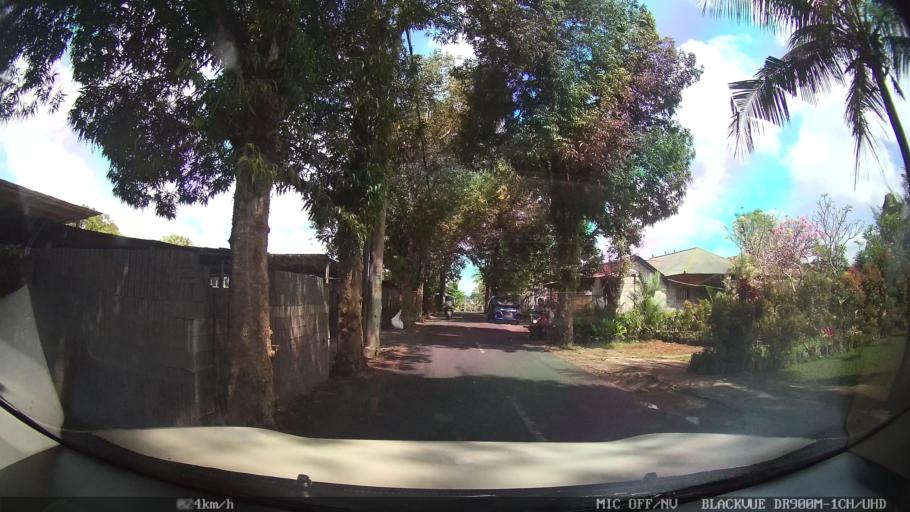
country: ID
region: Bali
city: Banjar Sedang
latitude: -8.5617
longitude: 115.2701
